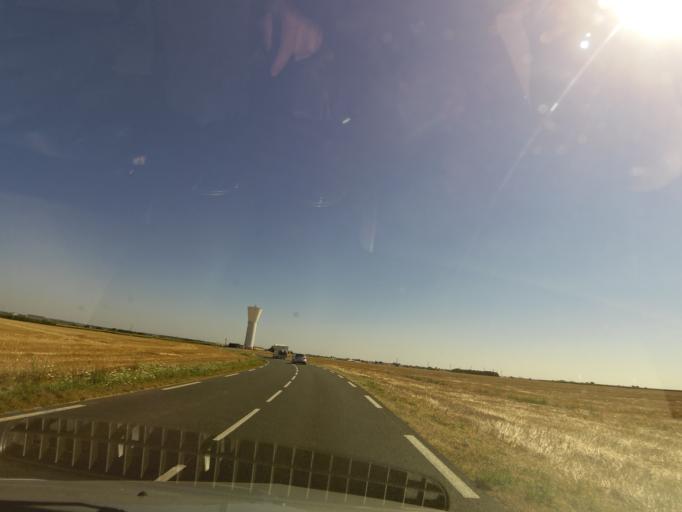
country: FR
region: Pays de la Loire
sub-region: Departement de la Vendee
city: Longeville-sur-Mer
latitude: 46.4240
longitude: -1.5129
